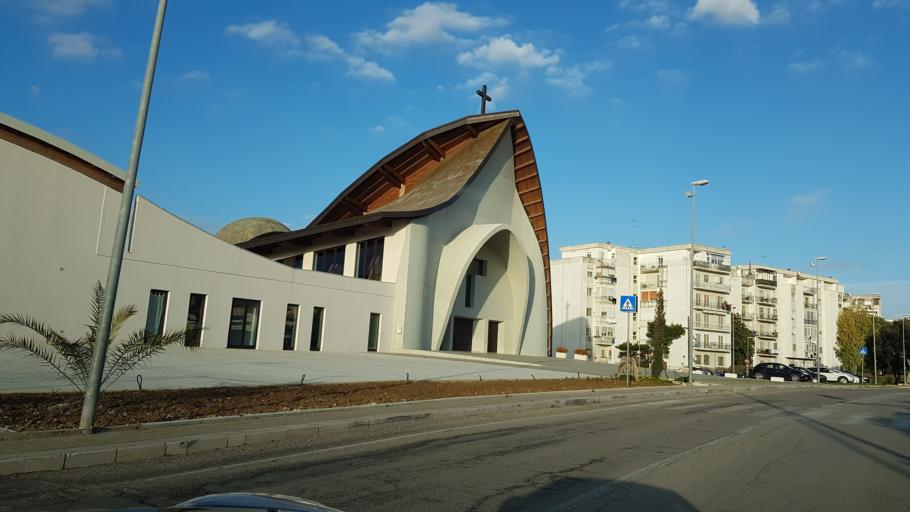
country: IT
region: Apulia
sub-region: Provincia di Brindisi
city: Brindisi
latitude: 40.6368
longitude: 17.9232
